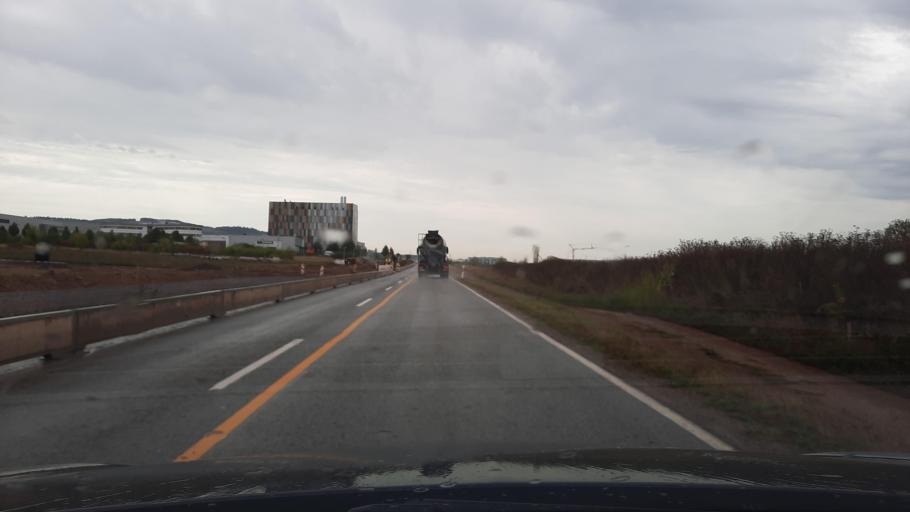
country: DE
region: Rheinland-Pfalz
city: Hetzerath
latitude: 49.8680
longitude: 6.8077
